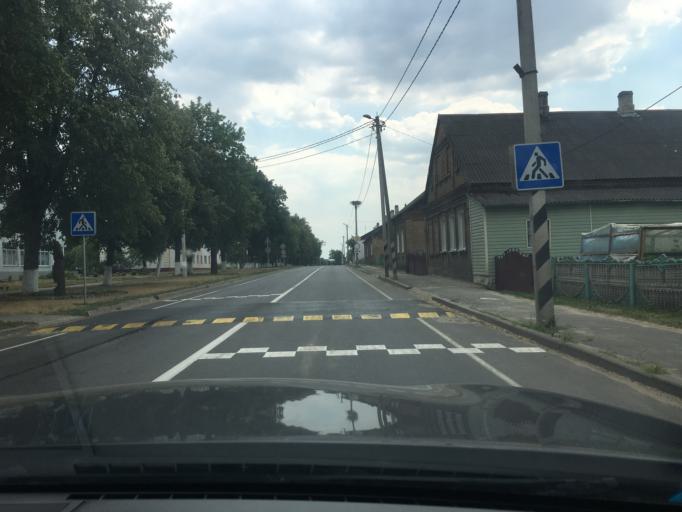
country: BY
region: Brest
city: Ruzhany
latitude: 52.8636
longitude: 24.8908
